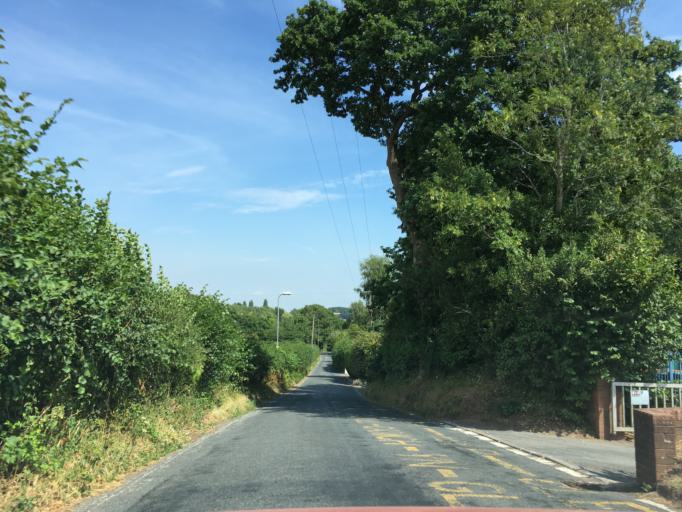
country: GB
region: Wales
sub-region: Newport
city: Langstone
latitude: 51.6131
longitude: -2.8933
